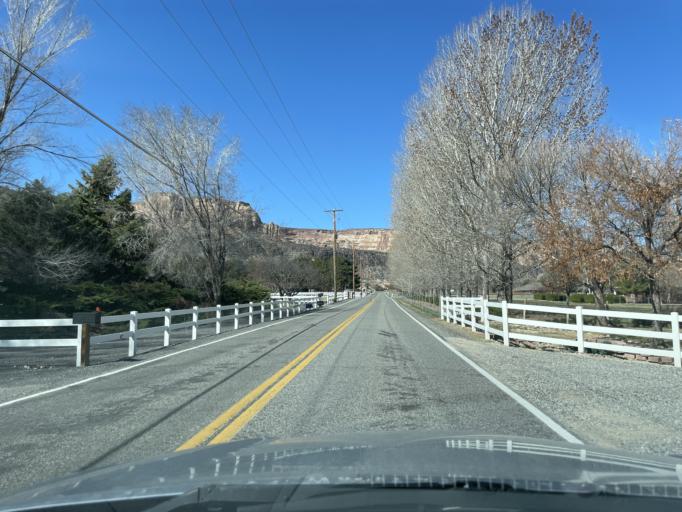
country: US
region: Colorado
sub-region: Mesa County
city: Redlands
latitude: 39.0742
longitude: -108.6591
